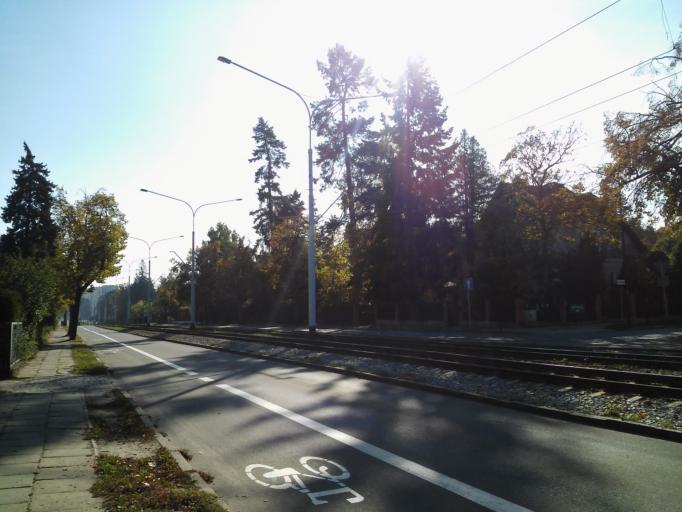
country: PL
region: Pomeranian Voivodeship
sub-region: Sopot
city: Sopot
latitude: 54.4047
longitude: 18.5643
